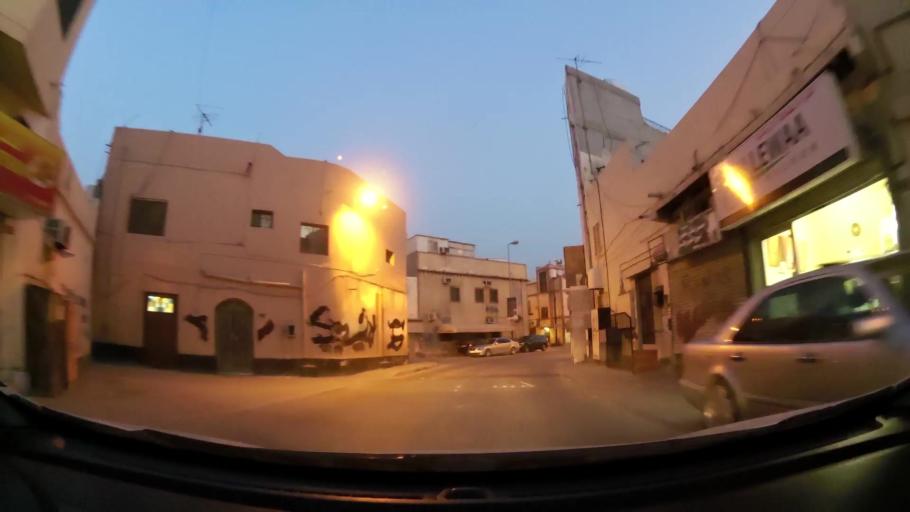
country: BH
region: Manama
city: Jidd Hafs
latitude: 26.2056
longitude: 50.5510
